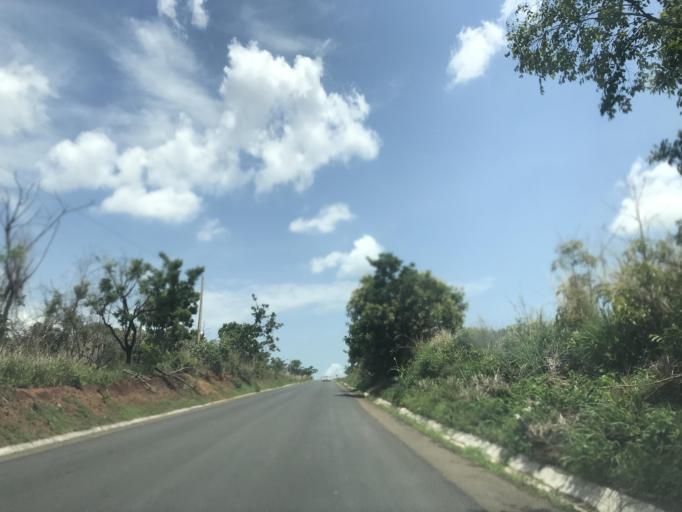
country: BR
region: Goias
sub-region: Bela Vista De Goias
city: Bela Vista de Goias
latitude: -17.0814
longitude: -48.6560
